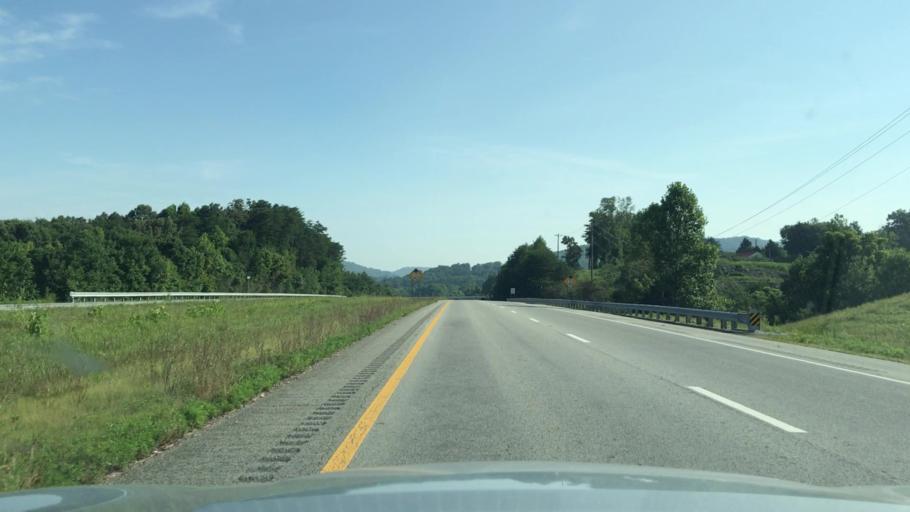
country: US
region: Tennessee
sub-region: Overton County
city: Livingston
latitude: 36.3550
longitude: -85.3433
